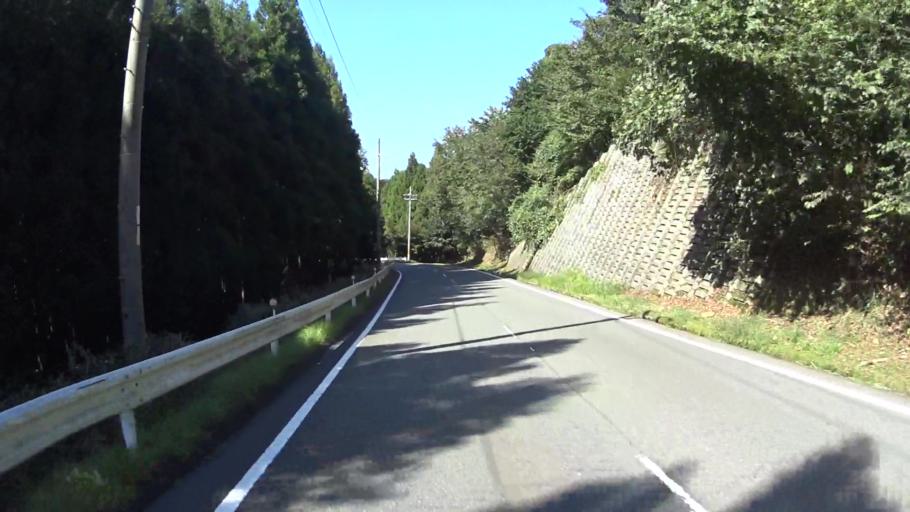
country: JP
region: Hyogo
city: Toyooka
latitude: 35.5360
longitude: 134.9789
